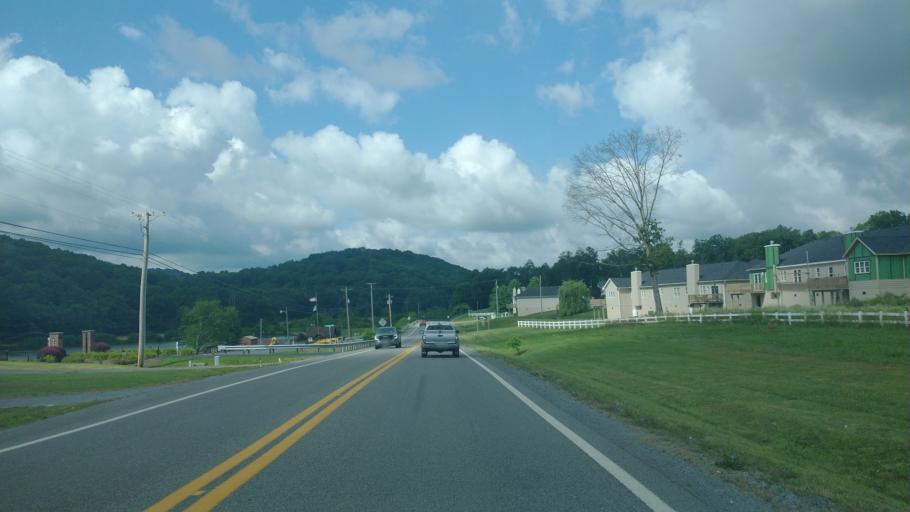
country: US
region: West Virginia
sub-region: Mercer County
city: Princeton
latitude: 37.3376
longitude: -81.1686
